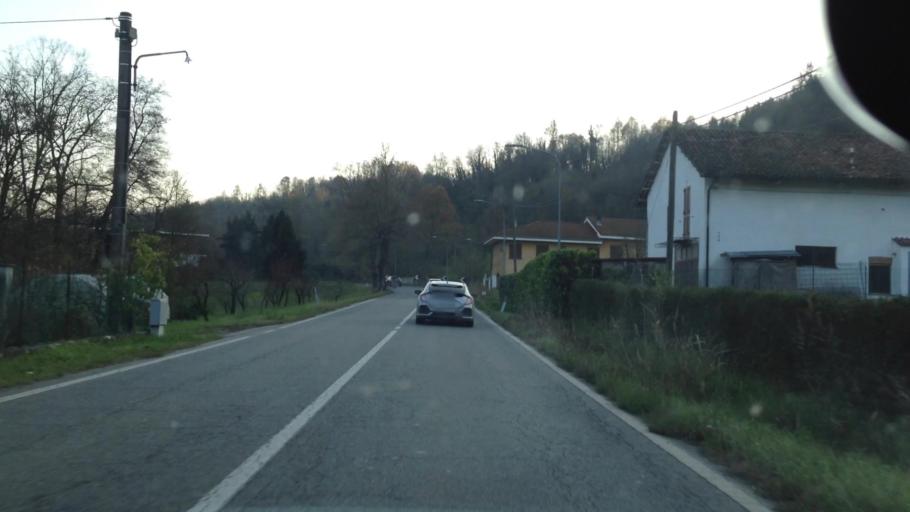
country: IT
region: Piedmont
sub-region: Provincia di Torino
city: Cavagnolo
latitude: 45.1366
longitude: 8.0551
